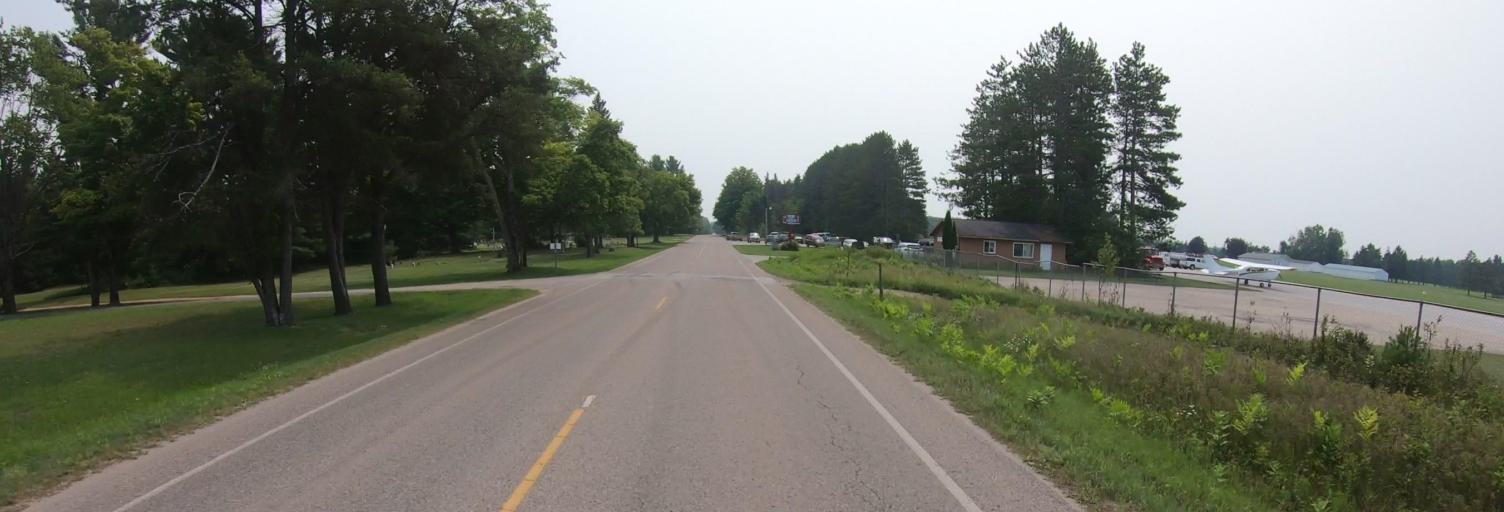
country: CA
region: Ontario
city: Thessalon
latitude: 46.0098
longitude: -83.7384
